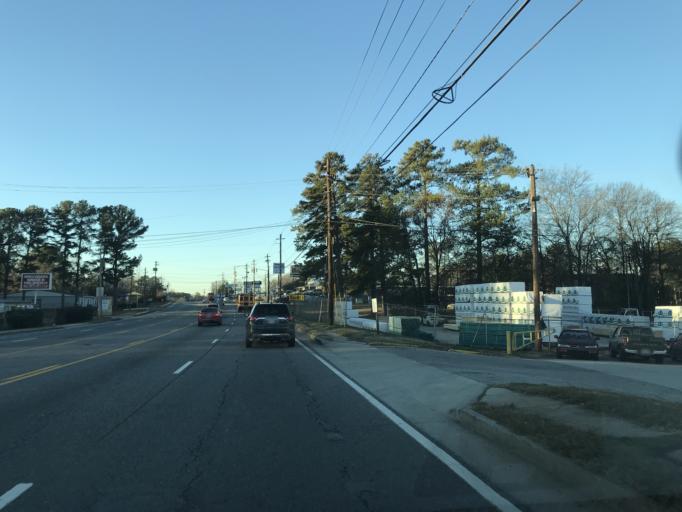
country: US
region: Georgia
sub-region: DeKalb County
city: Tucker
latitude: 33.8442
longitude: -84.2319
